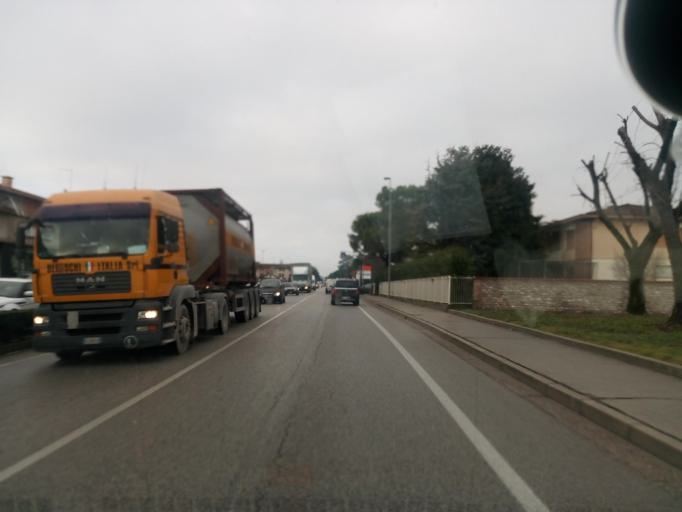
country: IT
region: Veneto
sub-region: Provincia di Vicenza
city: Sandrigo
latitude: 45.6627
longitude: 11.6043
